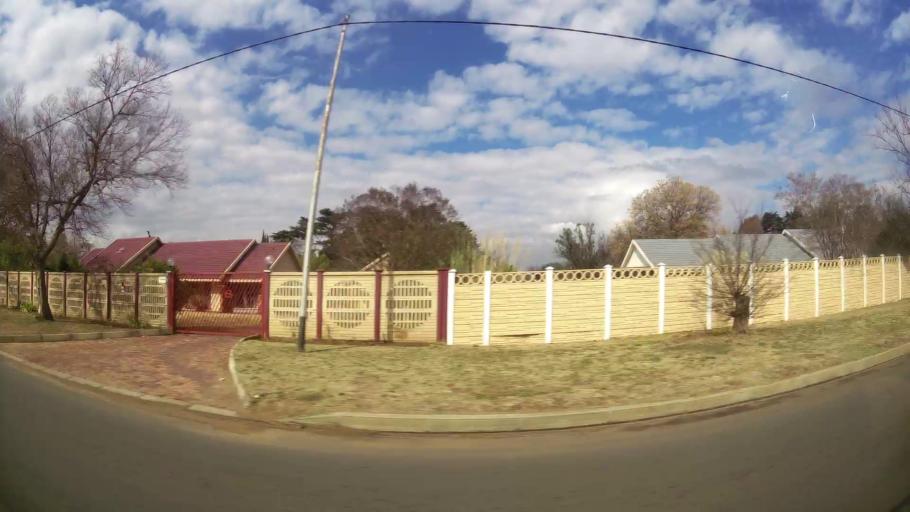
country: ZA
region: Gauteng
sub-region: Sedibeng District Municipality
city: Vereeniging
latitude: -26.6596
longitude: 27.9853
